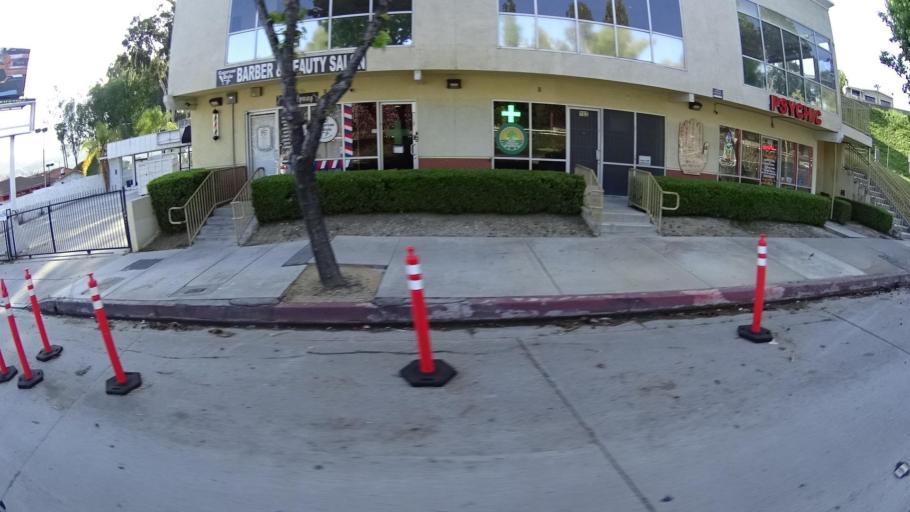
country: US
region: California
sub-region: Los Angeles County
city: South San Jose Hills
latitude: 34.0237
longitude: -117.9179
